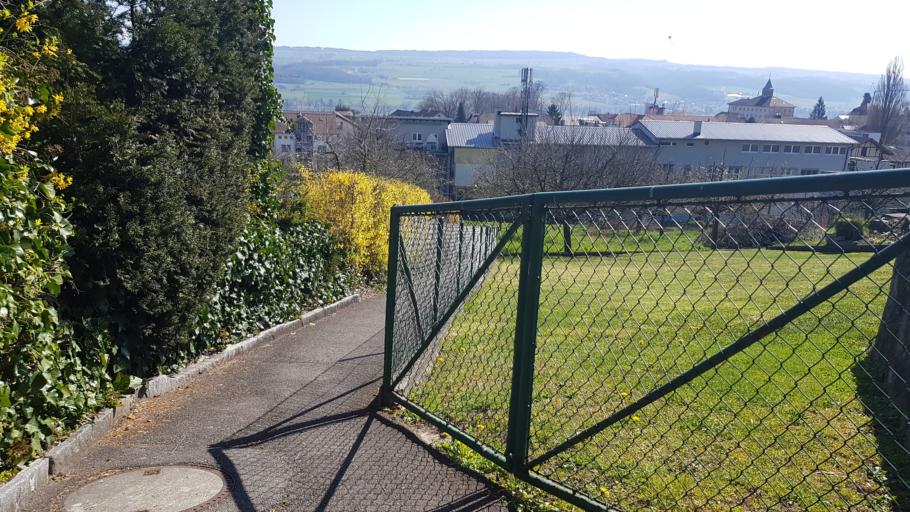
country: CH
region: Aargau
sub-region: Bezirk Kulm
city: Reinach
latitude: 47.2680
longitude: 8.2003
